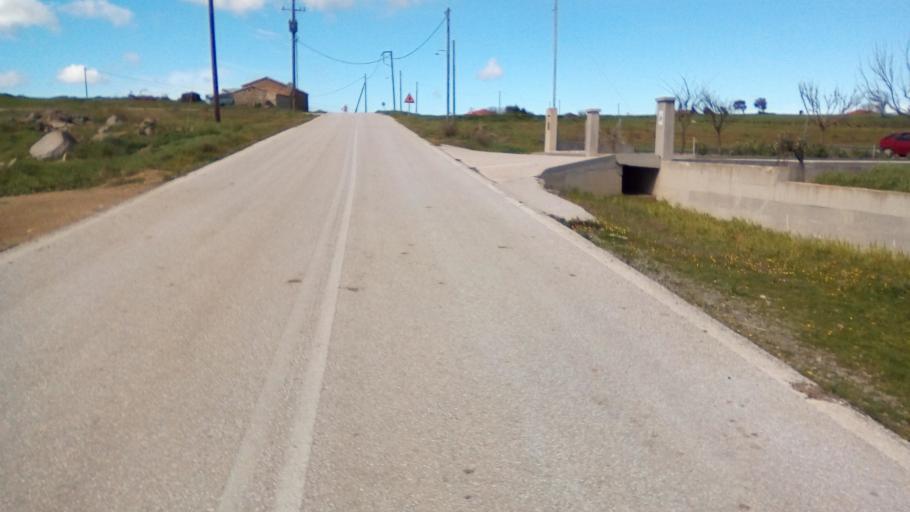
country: GR
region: North Aegean
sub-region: Nomos Lesvou
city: Myrina
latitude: 39.9293
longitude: 25.2321
